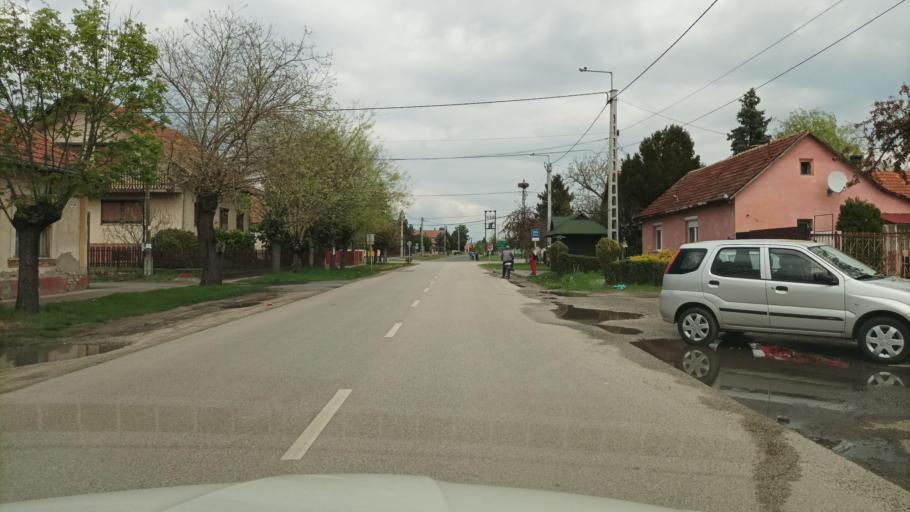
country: HU
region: Pest
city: Tortel
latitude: 47.1223
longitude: 19.9353
